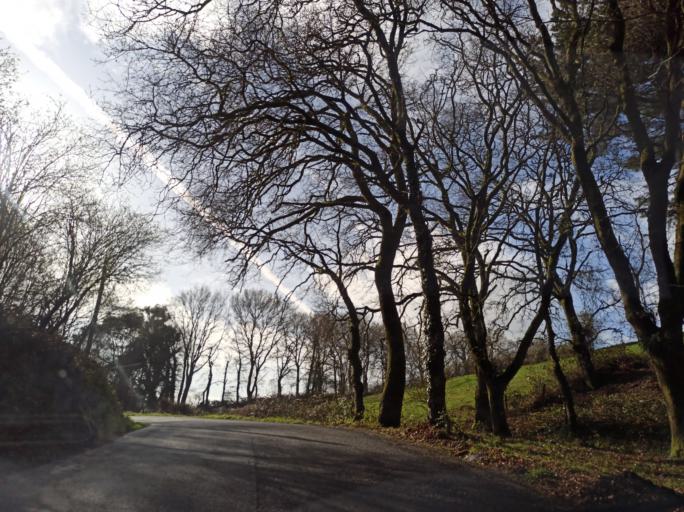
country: ES
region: Galicia
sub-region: Provincia da Coruna
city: Sobrado
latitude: 43.0900
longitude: -7.9695
